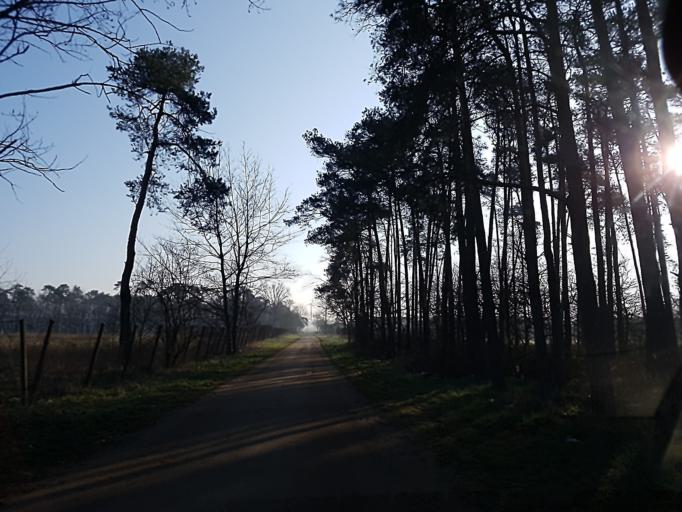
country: DE
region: Brandenburg
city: Finsterwalde
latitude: 51.6321
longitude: 13.7529
